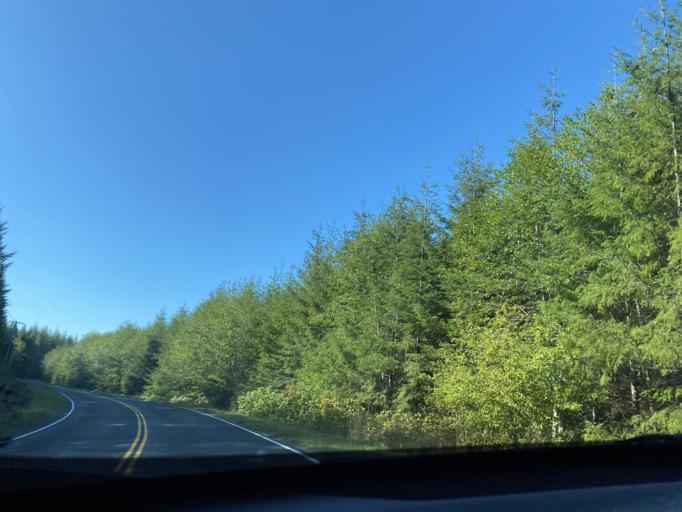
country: US
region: Washington
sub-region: Clallam County
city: Forks
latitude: 47.9504
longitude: -124.4776
